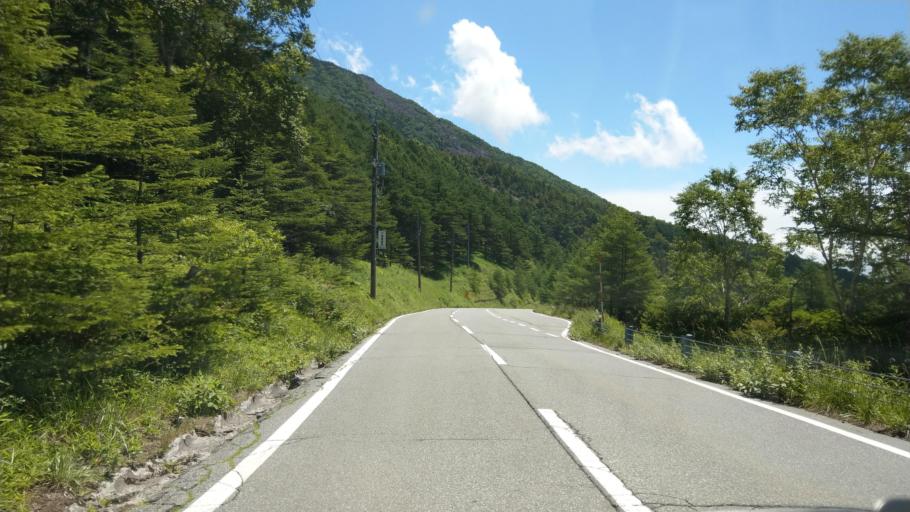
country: JP
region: Nagano
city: Komoro
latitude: 36.4031
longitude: 138.4705
